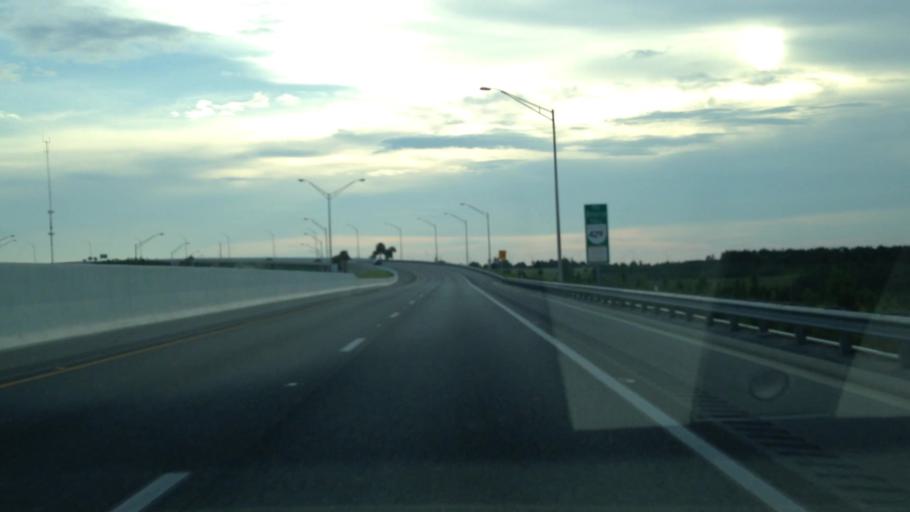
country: US
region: Florida
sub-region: Orange County
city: South Apopka
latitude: 28.6534
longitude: -81.5375
